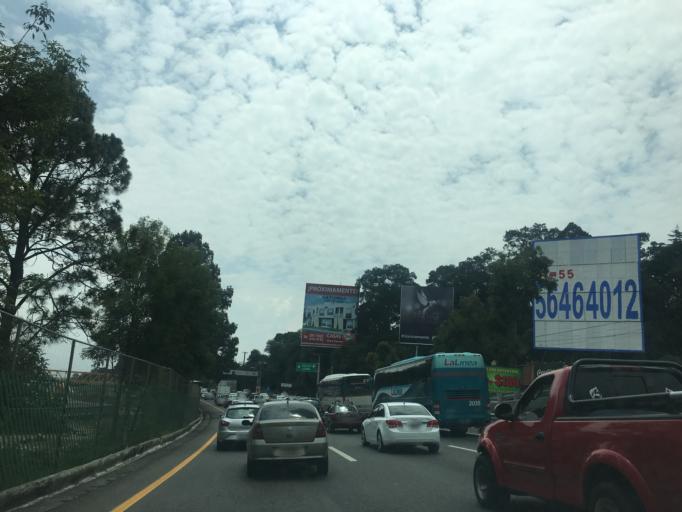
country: MX
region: Morelos
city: San Jeronimo Acazulco
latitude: 19.2924
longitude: -99.4301
